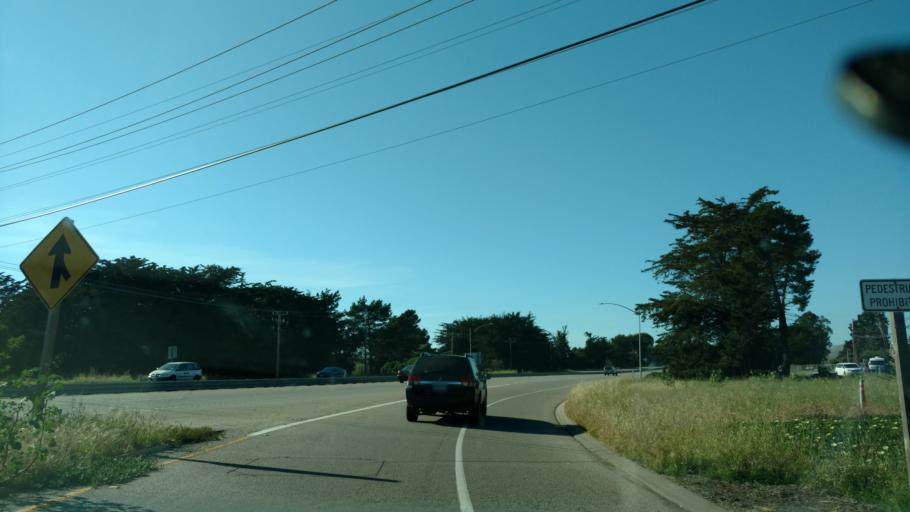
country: US
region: California
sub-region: San Luis Obispo County
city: Morro Bay
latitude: 35.3756
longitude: -120.8532
